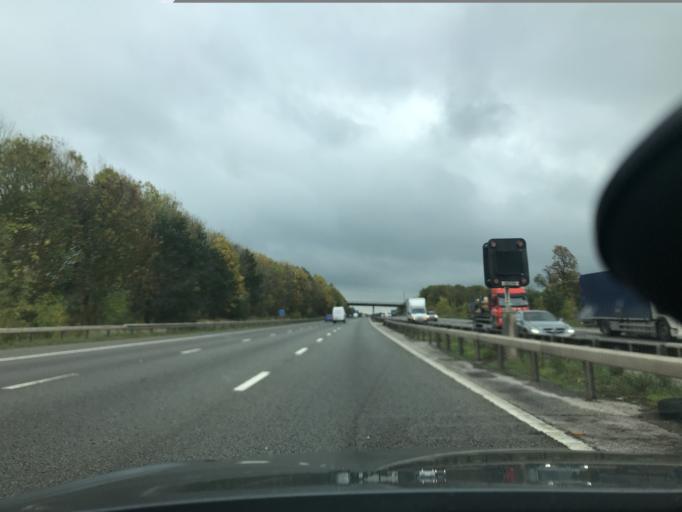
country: GB
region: England
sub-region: Warwickshire
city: Wroxall
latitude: 52.3209
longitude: -1.7212
